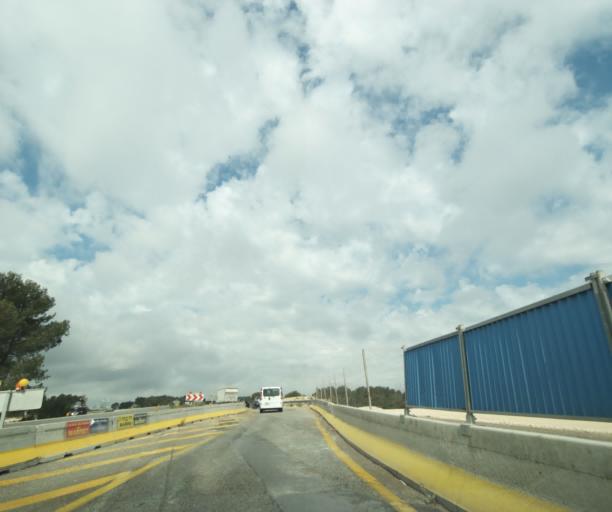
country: FR
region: Provence-Alpes-Cote d'Azur
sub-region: Departement des Bouches-du-Rhone
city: Les Pennes-Mirabeau
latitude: 43.4565
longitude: 5.3250
